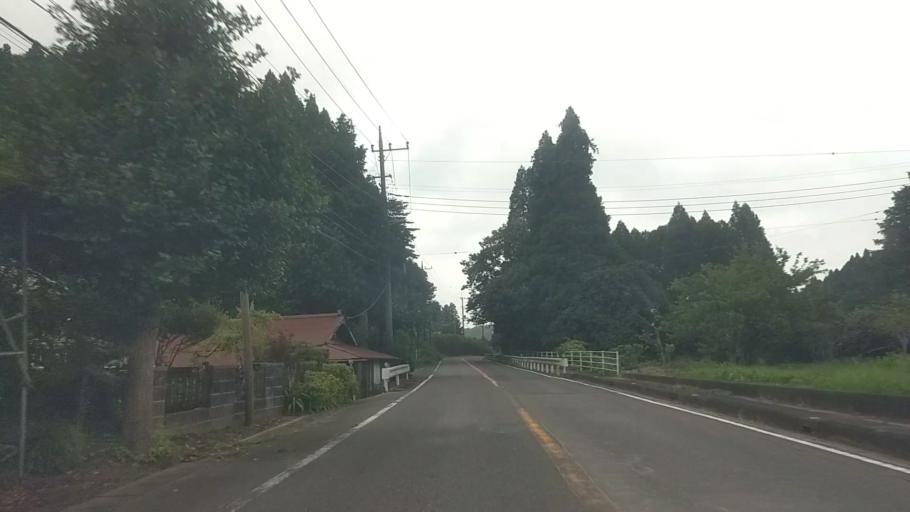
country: JP
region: Chiba
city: Katsuura
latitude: 35.2450
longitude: 140.1925
